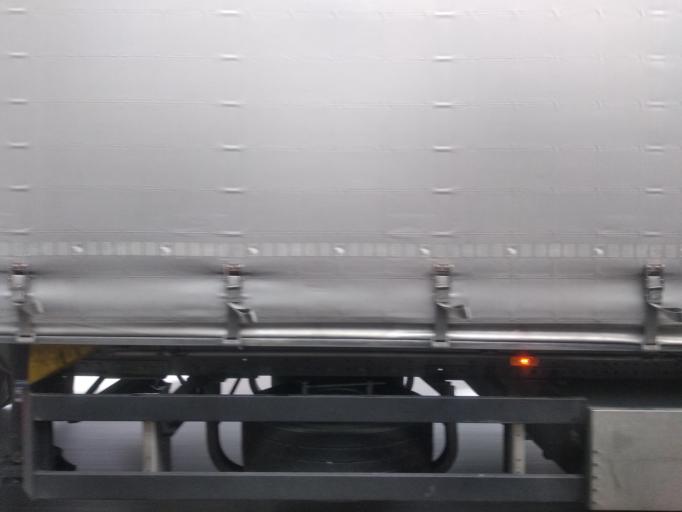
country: CH
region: Zurich
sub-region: Bezirk Winterthur
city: Wiesendangen / Wiesendangen (Dorf)
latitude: 47.5305
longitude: 8.8153
